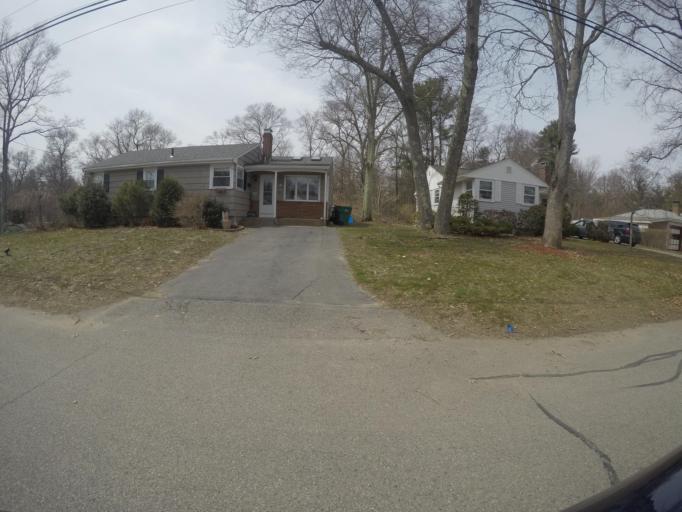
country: US
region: Massachusetts
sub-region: Bristol County
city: Easton
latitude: 42.0610
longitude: -71.1106
